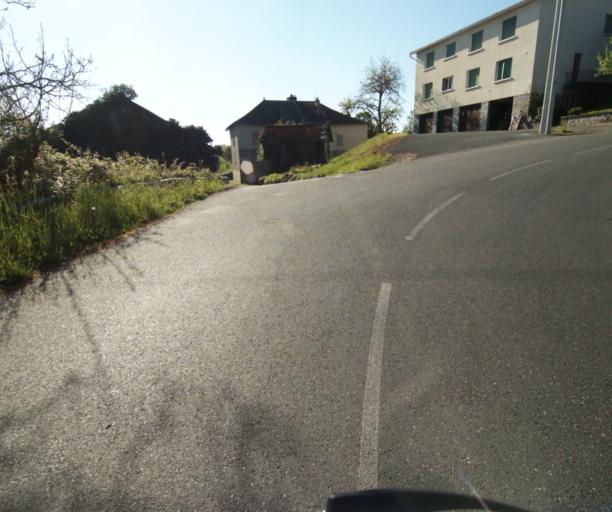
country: FR
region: Limousin
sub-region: Departement de la Correze
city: Tulle
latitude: 45.2717
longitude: 1.7864
